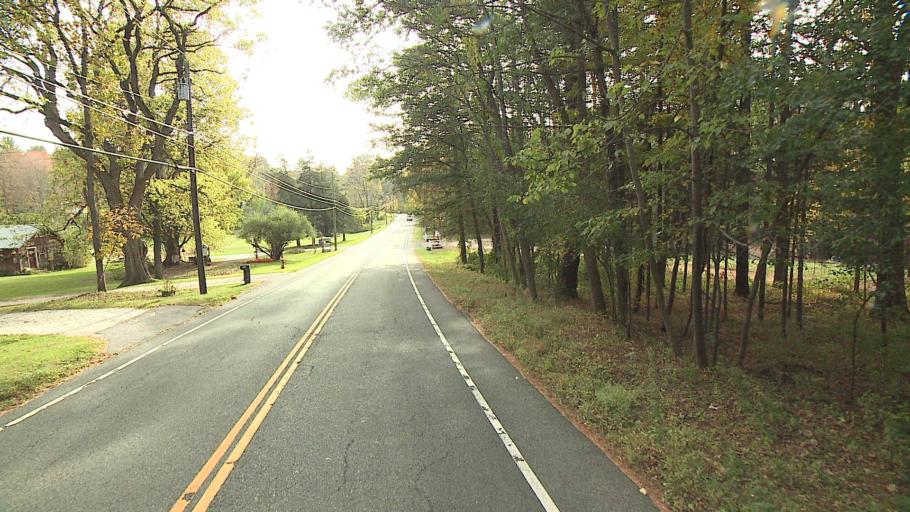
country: US
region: Connecticut
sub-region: Litchfield County
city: Canaan
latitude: 42.0196
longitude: -73.3486
